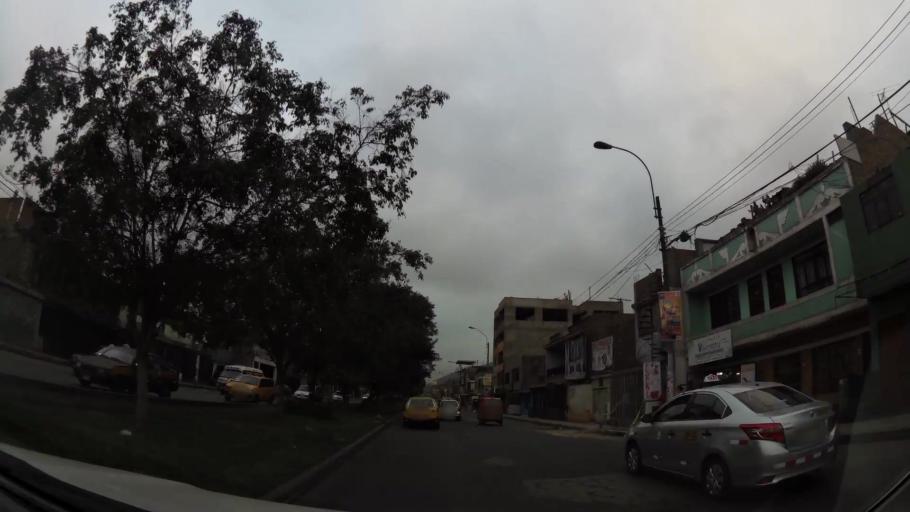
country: PE
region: Lima
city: Lima
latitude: -12.0180
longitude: -77.0122
